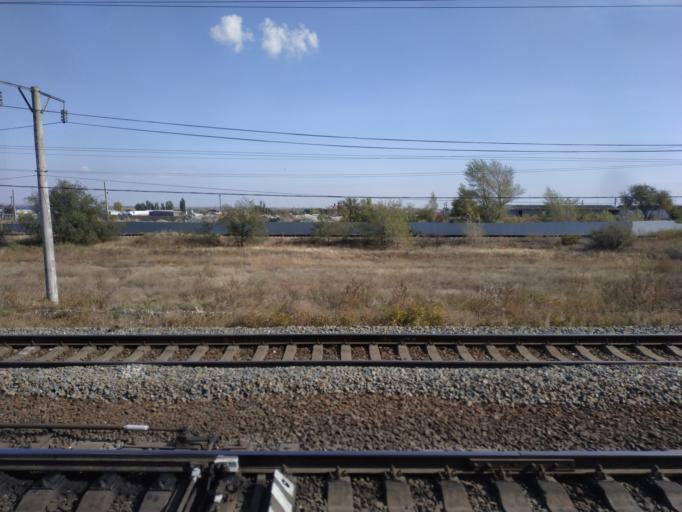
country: RU
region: Volgograd
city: Gumrak
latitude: 48.7910
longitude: 44.3673
